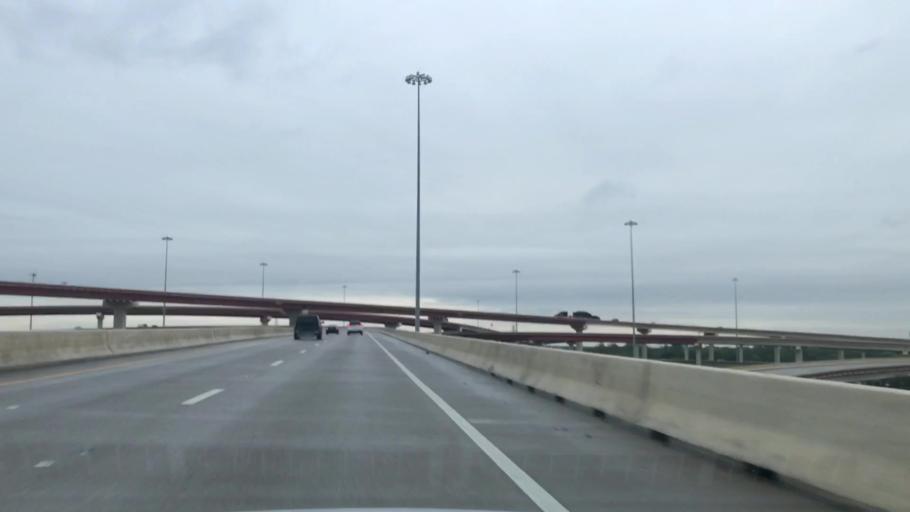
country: US
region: Texas
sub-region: Dallas County
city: Carrollton
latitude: 32.9842
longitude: -96.9335
